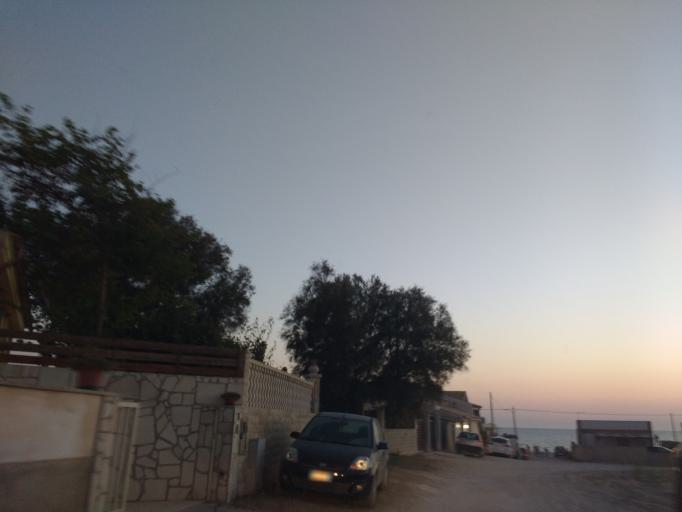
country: IT
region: Sicily
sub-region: Ragusa
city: Cava d'Aliga
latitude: 36.7341
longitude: 14.6816
